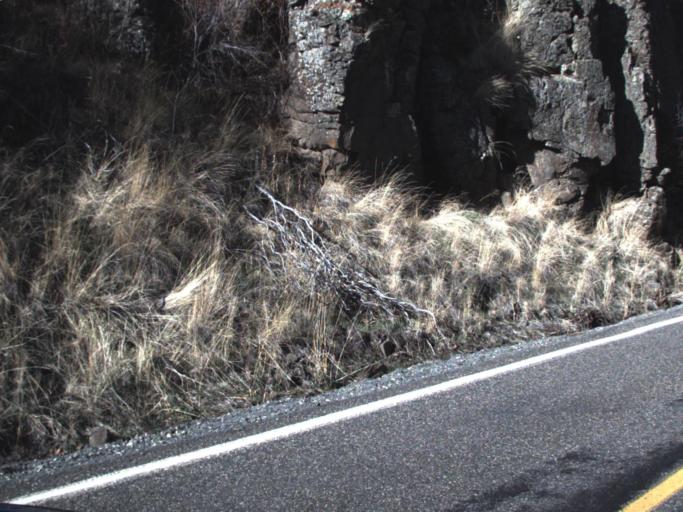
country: US
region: Washington
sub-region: Asotin County
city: Asotin
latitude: 46.0549
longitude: -117.2384
